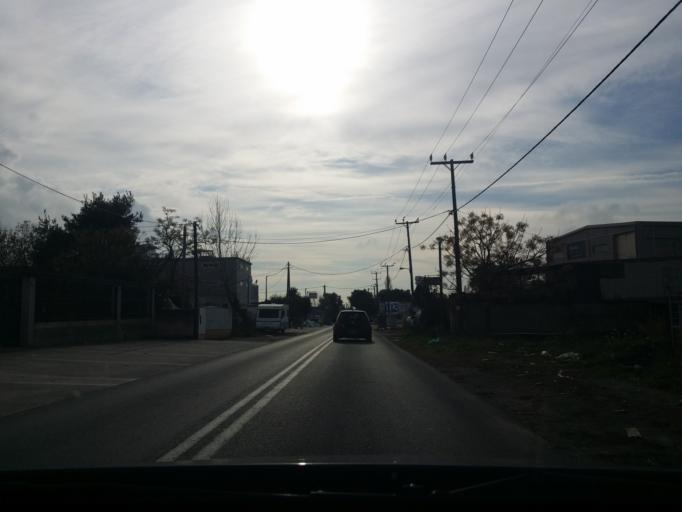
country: GR
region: Attica
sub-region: Nomarchia Athinas
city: Metamorfosi
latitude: 38.0835
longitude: 23.7668
